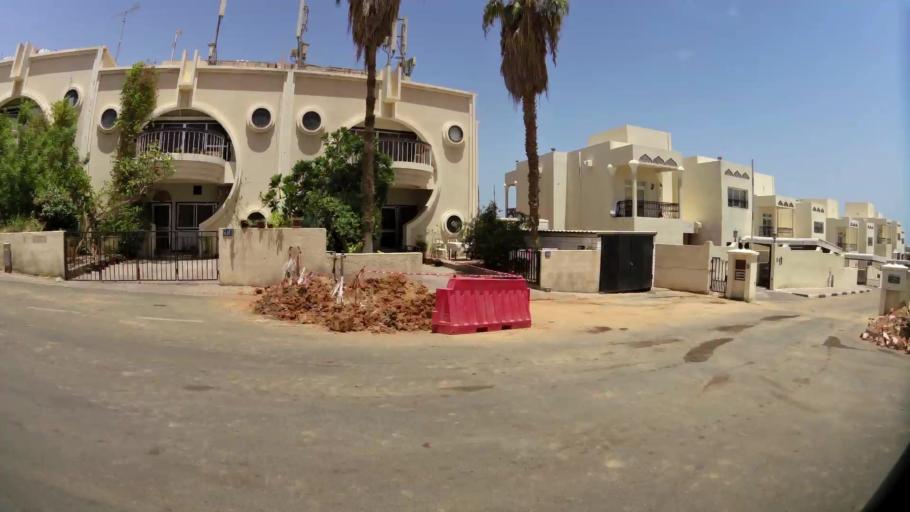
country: OM
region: Muhafazat Masqat
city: Bawshar
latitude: 23.6099
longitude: 58.4711
